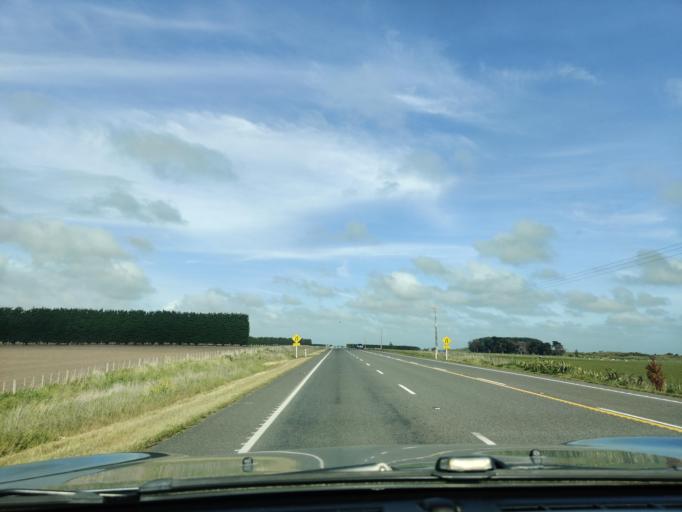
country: NZ
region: Manawatu-Wanganui
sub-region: Wanganui District
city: Wanganui
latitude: -39.9845
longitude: 175.1535
